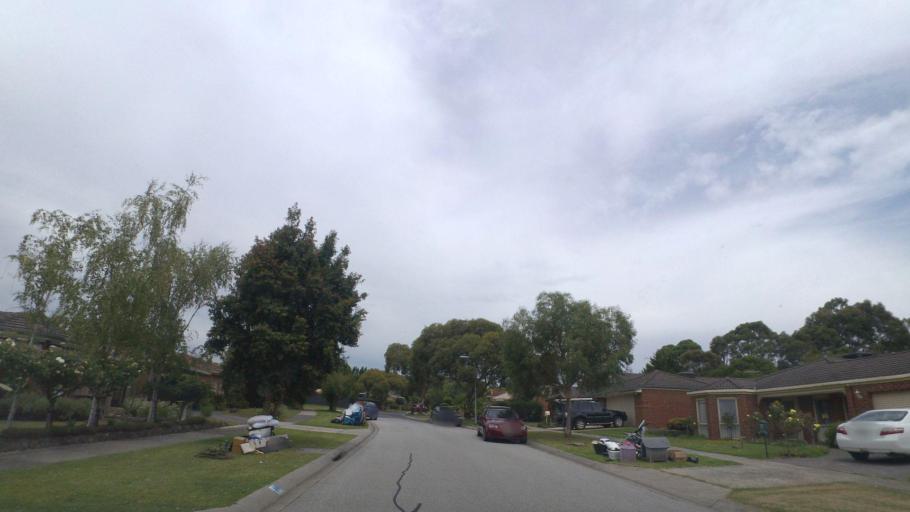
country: AU
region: Victoria
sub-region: Yarra Ranges
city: Lilydale
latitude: -37.7718
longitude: 145.3491
